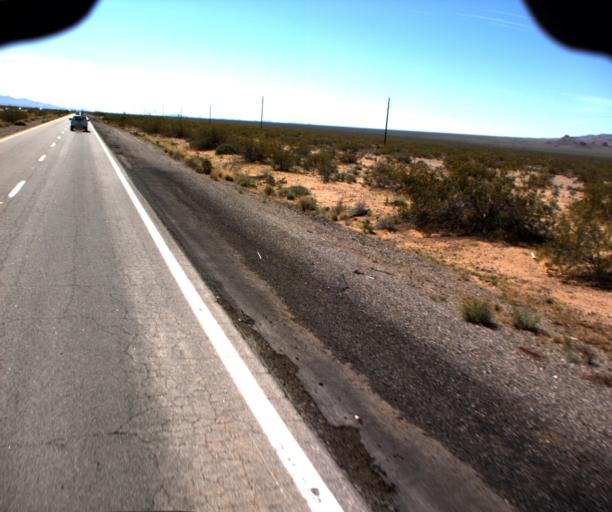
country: US
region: Arizona
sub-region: Mohave County
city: Dolan Springs
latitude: 35.6576
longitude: -114.4472
